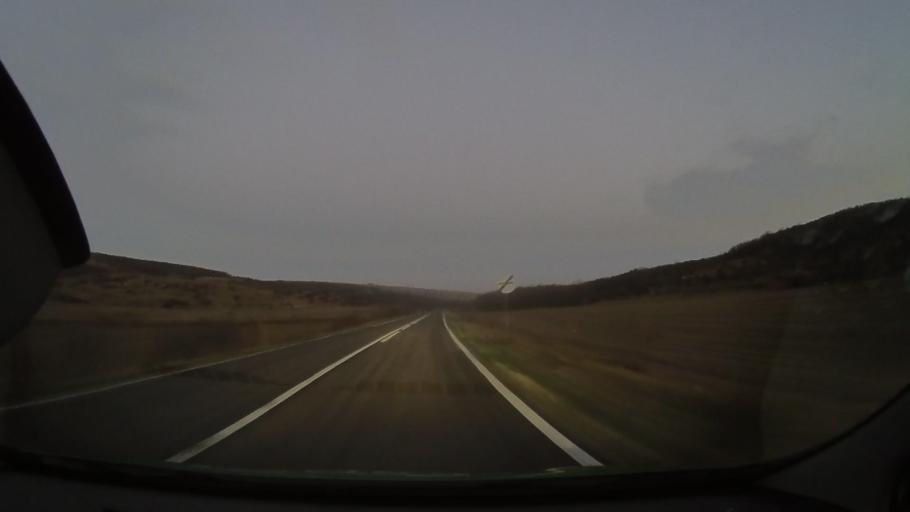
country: RO
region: Constanta
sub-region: Comuna Ion Corvin
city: Ion Corvin
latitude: 44.1111
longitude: 27.7654
